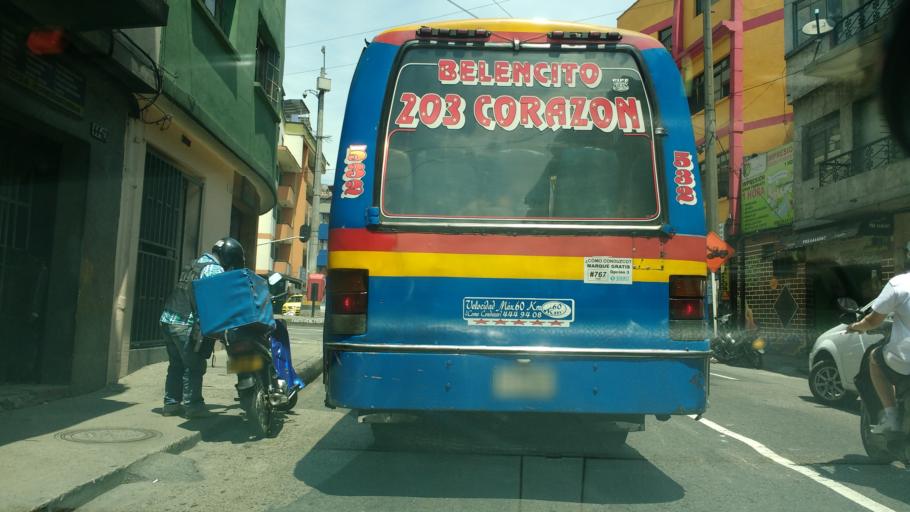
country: CO
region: Antioquia
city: Medellin
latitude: 6.2443
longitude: -75.5668
